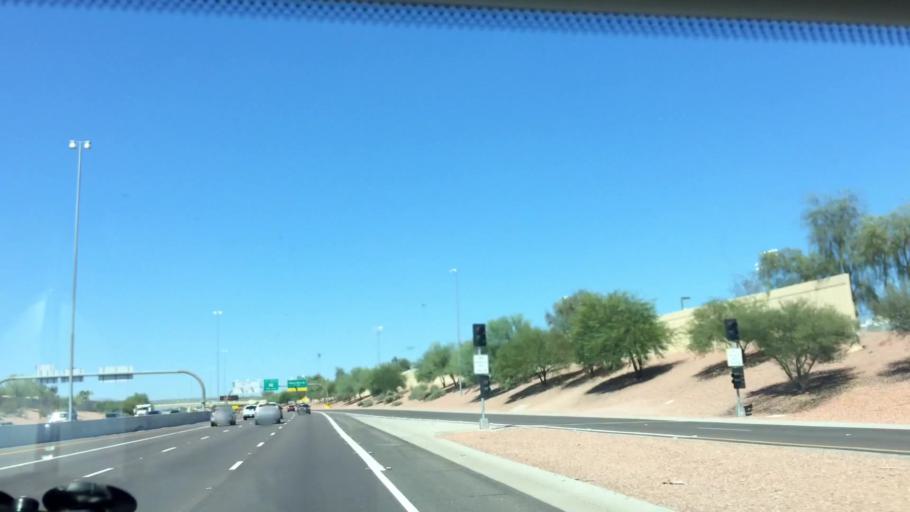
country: US
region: Arizona
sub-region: Maricopa County
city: Paradise Valley
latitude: 33.6443
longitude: -112.0035
